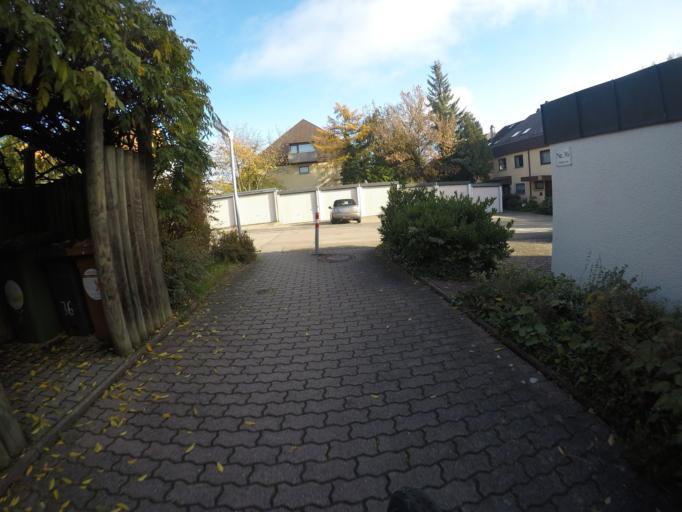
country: DE
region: Baden-Wuerttemberg
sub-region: Regierungsbezirk Stuttgart
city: Leinfelden-Echterdingen
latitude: 48.7257
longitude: 9.1383
